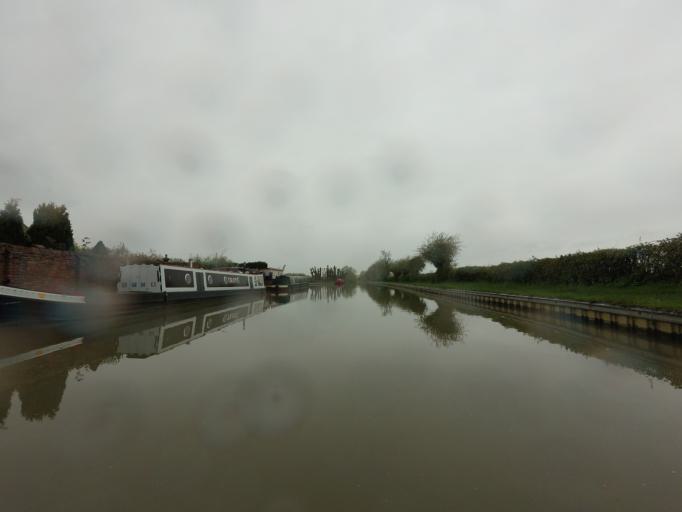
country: GB
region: England
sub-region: Milton Keynes
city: Castlethorpe
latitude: 52.1008
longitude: -0.8813
